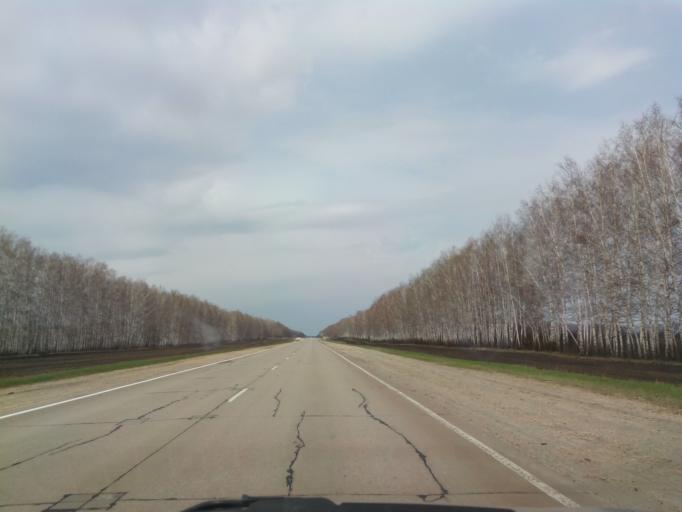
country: RU
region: Tambov
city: Satinka
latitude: 52.2003
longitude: 41.5721
